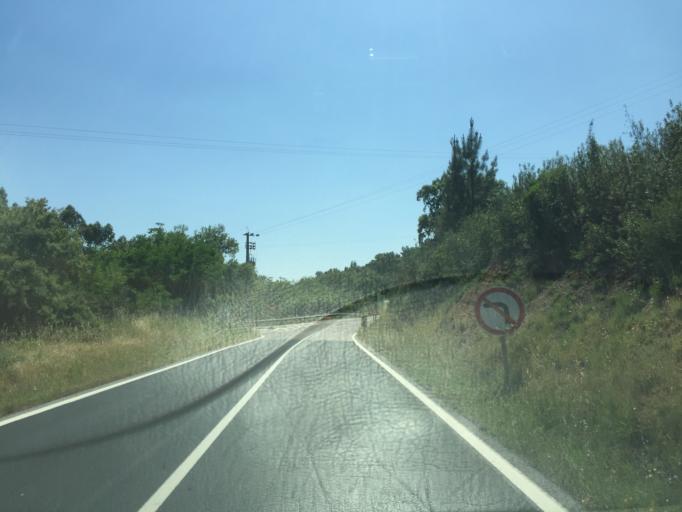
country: PT
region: Santarem
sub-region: Constancia
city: Constancia
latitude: 39.4757
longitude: -8.3472
